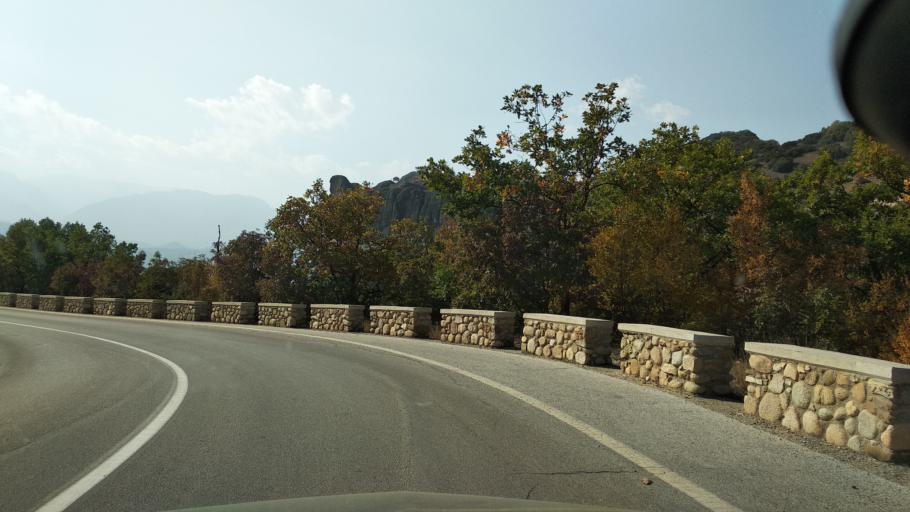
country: GR
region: Thessaly
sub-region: Trikala
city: Kastraki
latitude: 39.7249
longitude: 21.6371
